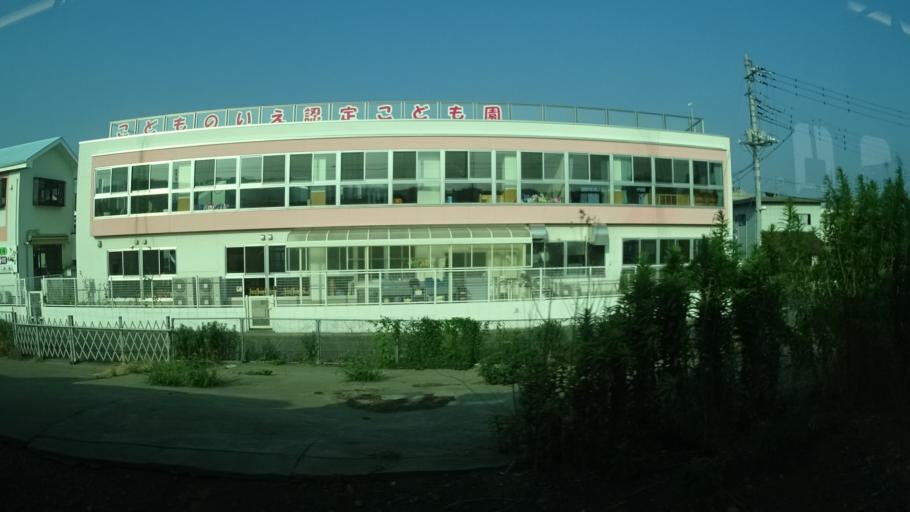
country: JP
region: Ibaraki
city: Hitachi
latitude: 36.6347
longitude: 140.6761
